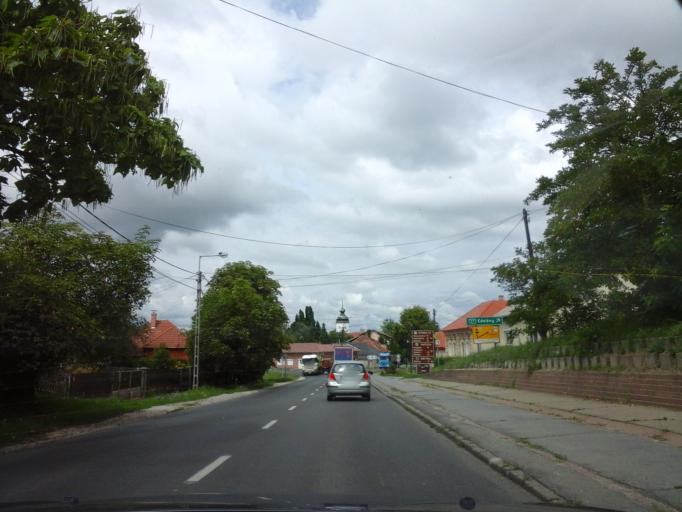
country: HU
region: Borsod-Abauj-Zemplen
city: Sajoszentpeter
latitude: 48.2147
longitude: 20.7267
